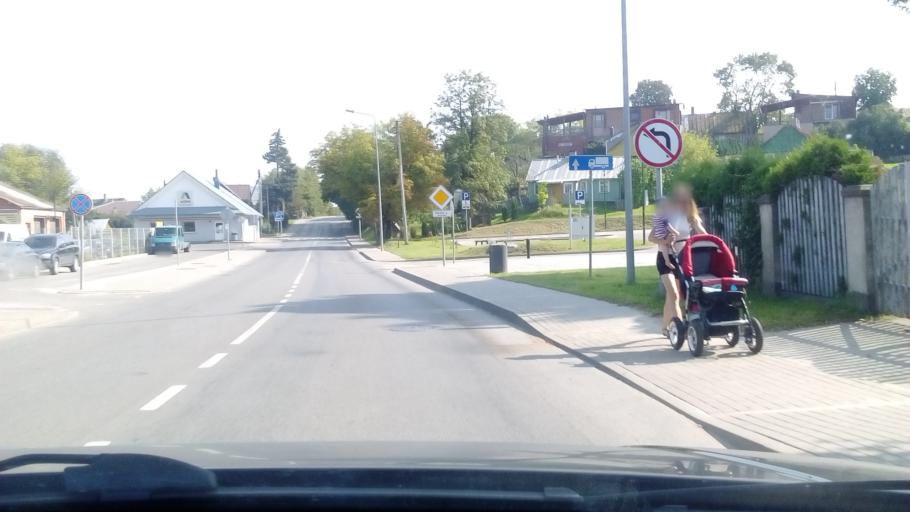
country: LT
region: Alytaus apskritis
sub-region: Alytus
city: Alytus
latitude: 54.4013
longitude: 24.0451
